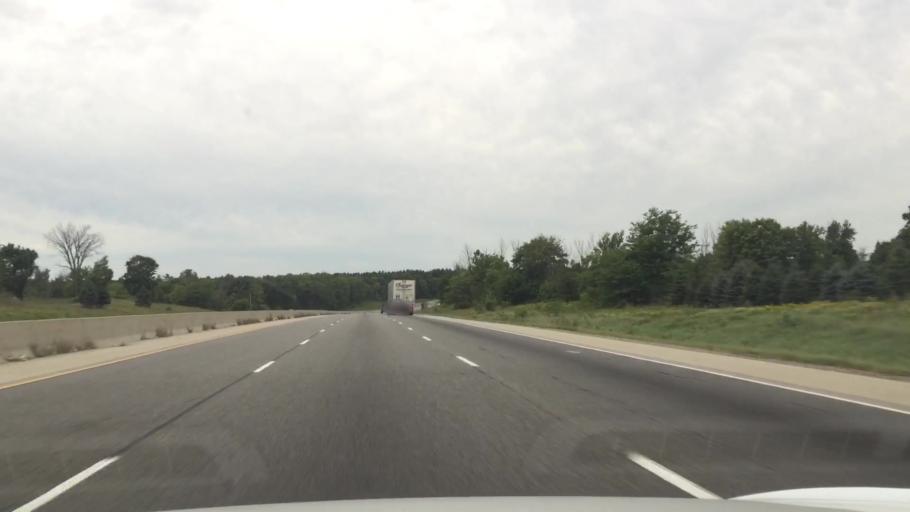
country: CA
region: Ontario
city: Kitchener
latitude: 43.2768
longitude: -80.5259
